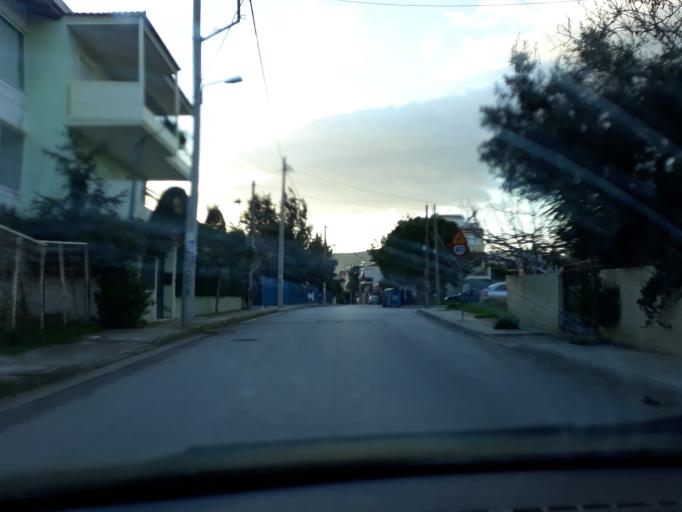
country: GR
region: Attica
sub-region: Nomarchia Anatolikis Attikis
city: Acharnes
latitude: 38.0856
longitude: 23.7169
